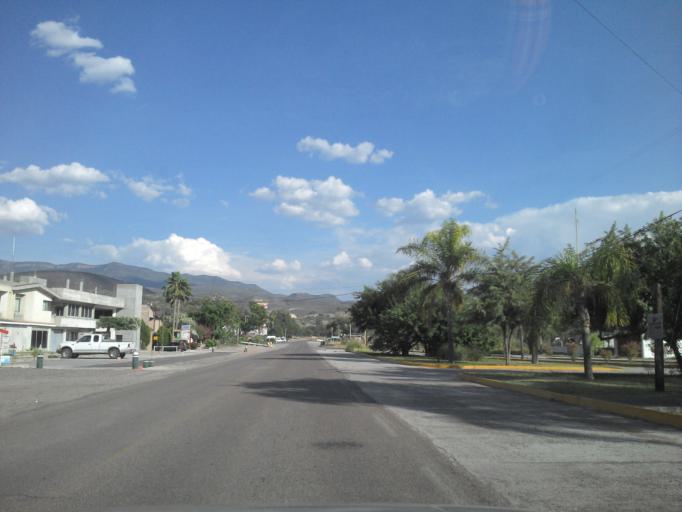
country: MX
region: Zacatecas
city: Juchipila
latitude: 21.2624
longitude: -103.1599
